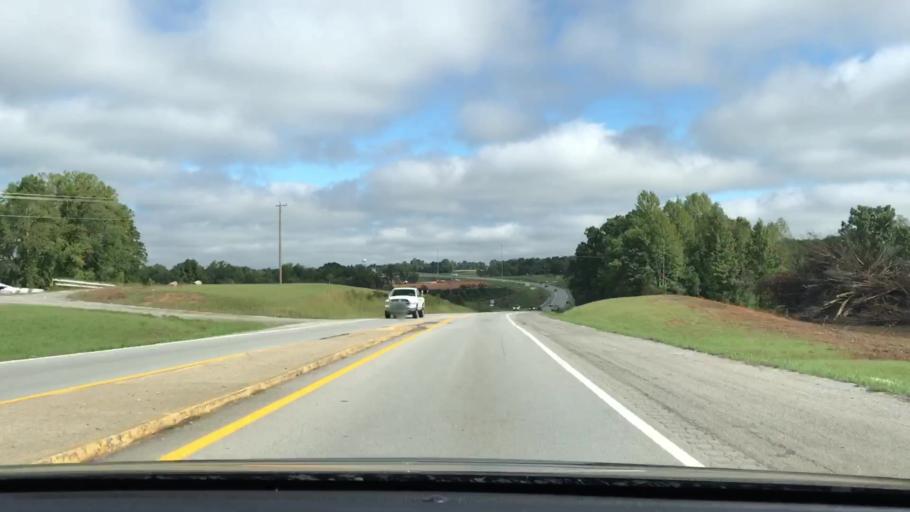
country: US
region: Kentucky
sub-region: Russell County
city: Russell Springs
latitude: 37.0395
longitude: -85.0740
